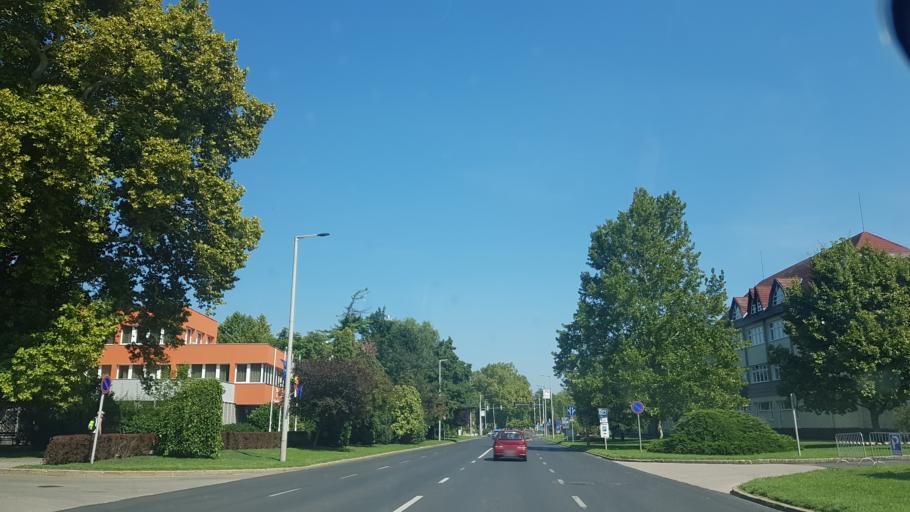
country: HU
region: Somogy
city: Nagyatad
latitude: 46.2298
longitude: 17.3591
